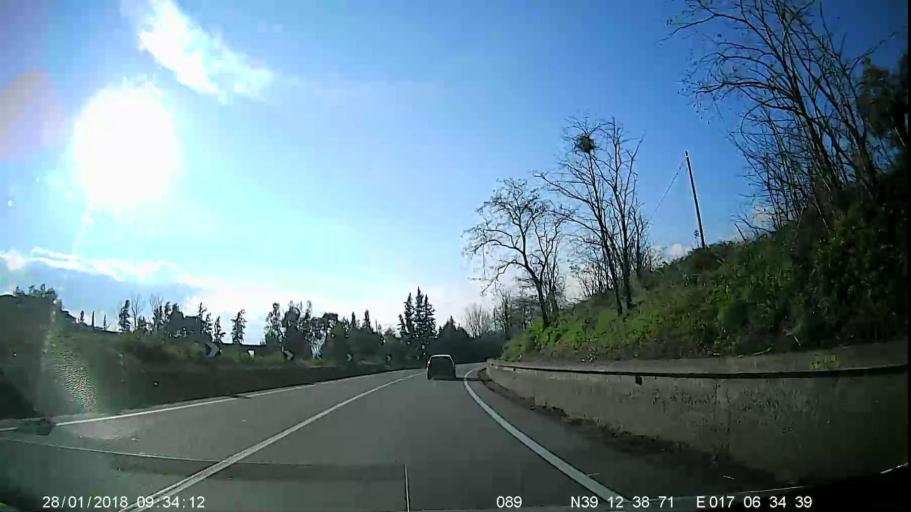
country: IT
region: Calabria
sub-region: Provincia di Crotone
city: Tronca
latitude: 39.2104
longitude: 17.1097
